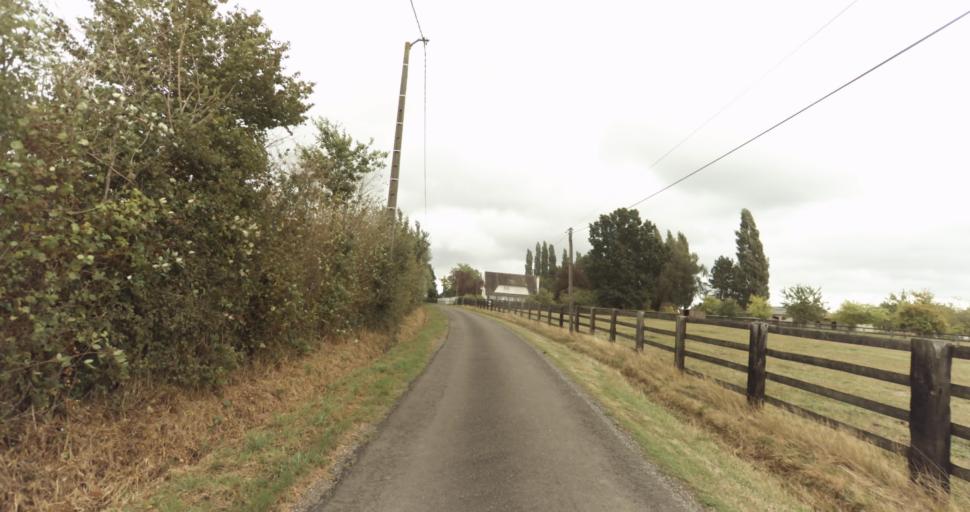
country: FR
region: Lower Normandy
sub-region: Departement de l'Orne
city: Sainte-Gauburge-Sainte-Colombe
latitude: 48.7198
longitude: 0.4619
